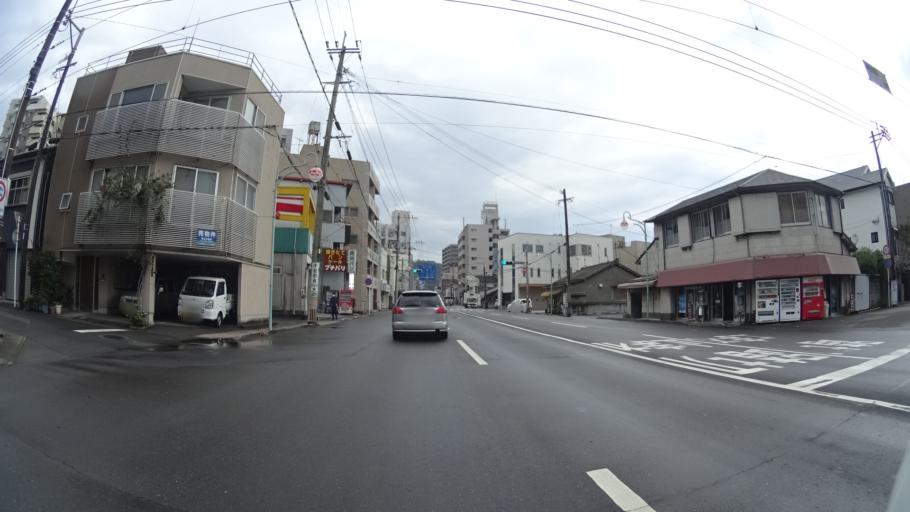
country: JP
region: Kagoshima
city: Kagoshima-shi
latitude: 31.6013
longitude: 130.5606
